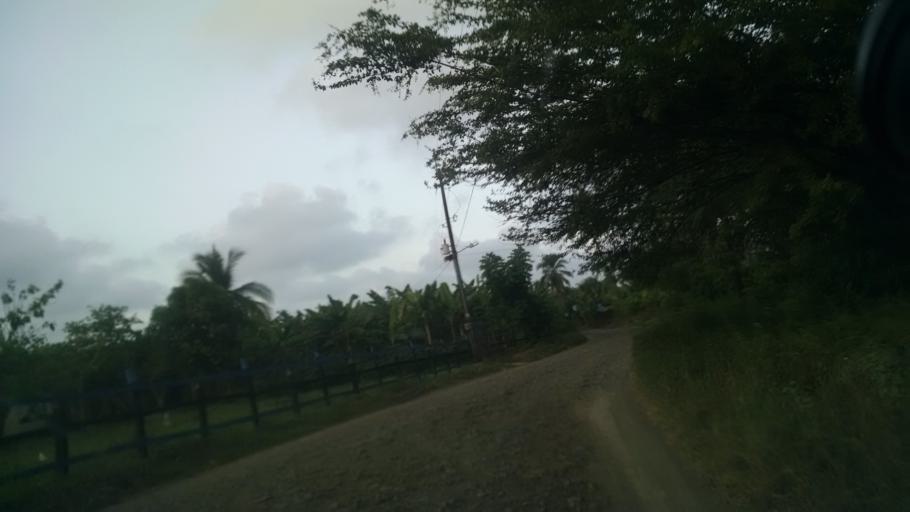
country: CO
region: Antioquia
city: San Juan de Uraba
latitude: 8.7326
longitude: -76.6060
